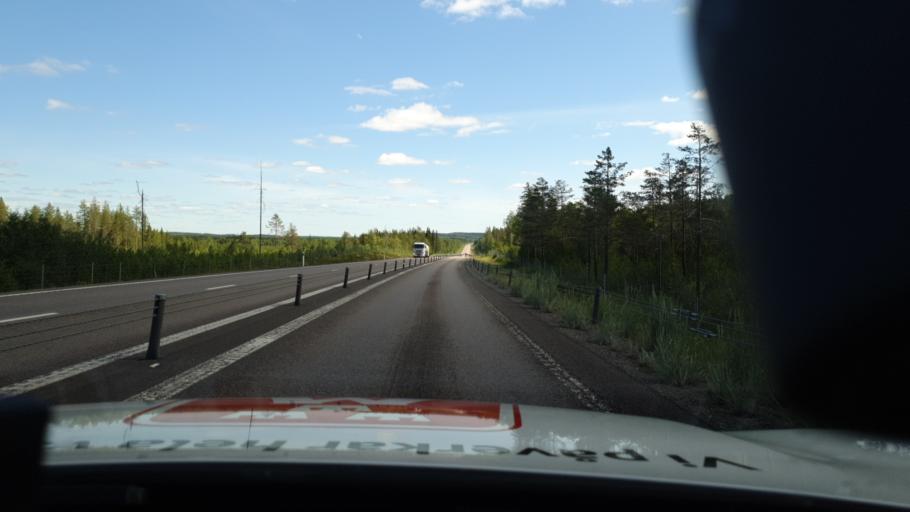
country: SE
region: Norrbotten
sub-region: Kalix Kommun
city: Toere
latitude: 65.9038
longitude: 22.8526
